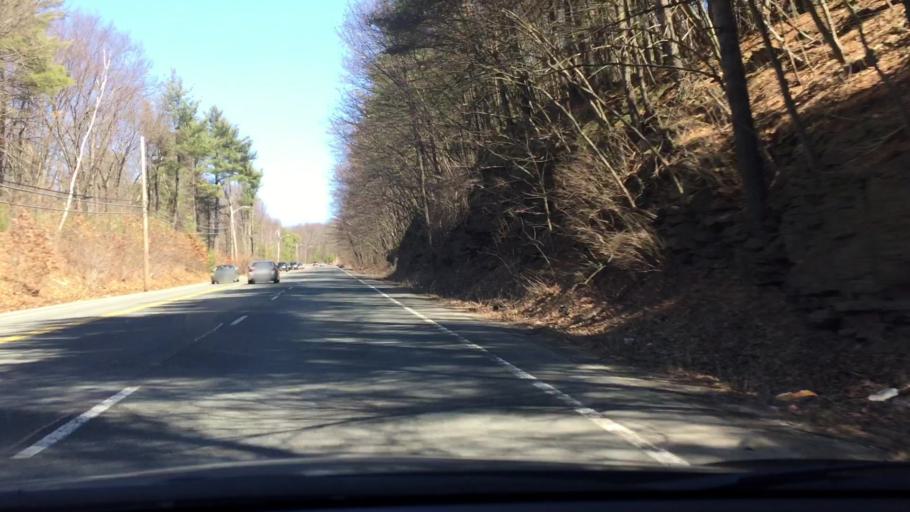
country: US
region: Massachusetts
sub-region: Hampden County
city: Holyoke
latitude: 42.1822
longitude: -72.6793
